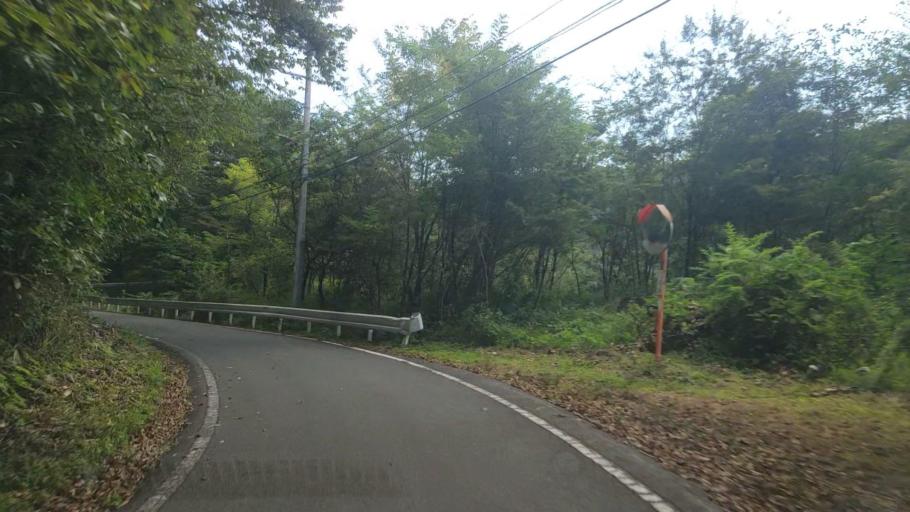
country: JP
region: Gunma
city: Nakanojomachi
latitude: 36.6546
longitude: 138.6341
